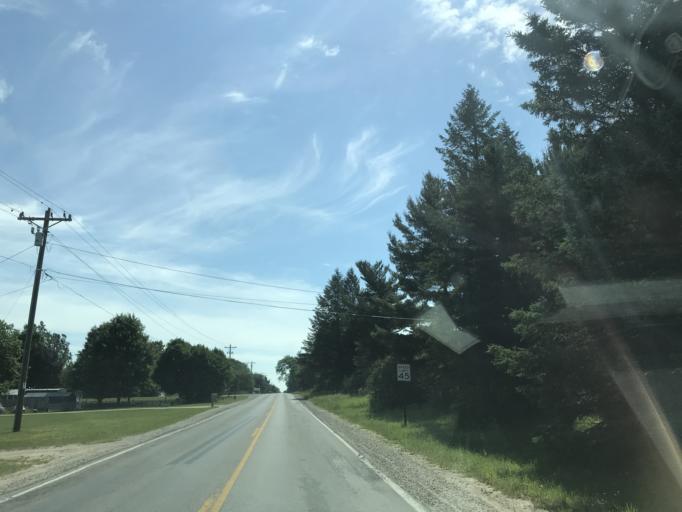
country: US
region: Michigan
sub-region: Grand Traverse County
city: Traverse City
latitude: 44.6576
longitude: -85.6857
